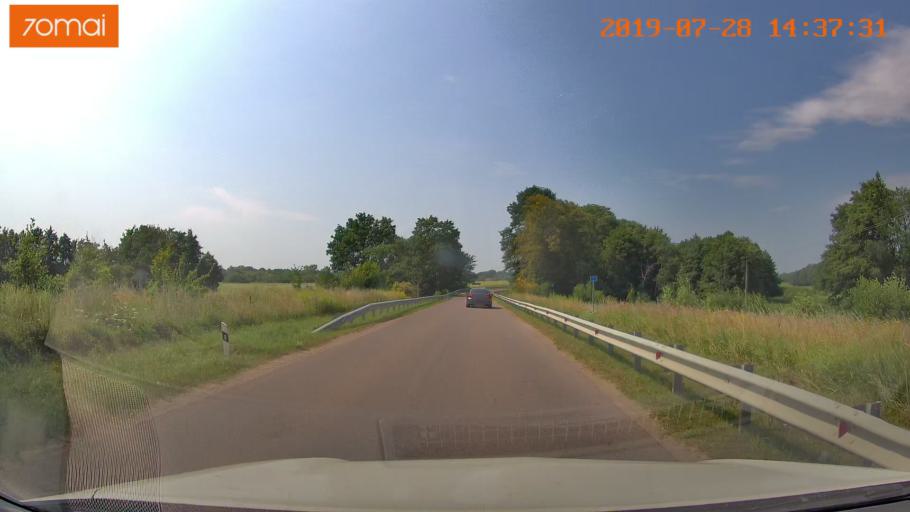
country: RU
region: Kaliningrad
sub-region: Gorod Kaliningrad
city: Yantarnyy
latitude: 54.8408
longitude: 19.9965
